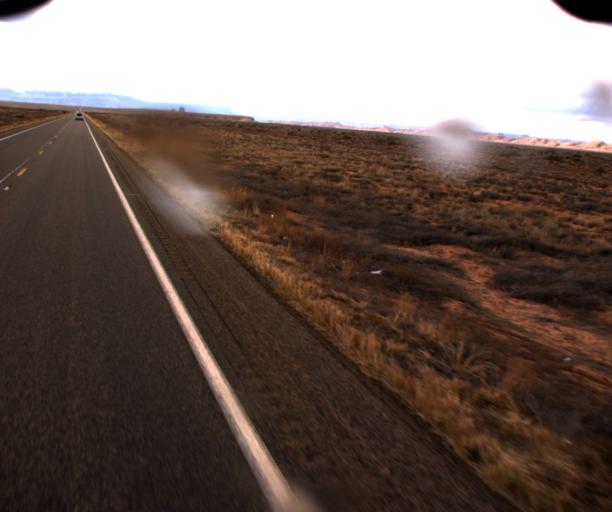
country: US
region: Arizona
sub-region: Navajo County
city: Kayenta
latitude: 36.7686
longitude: -110.0292
